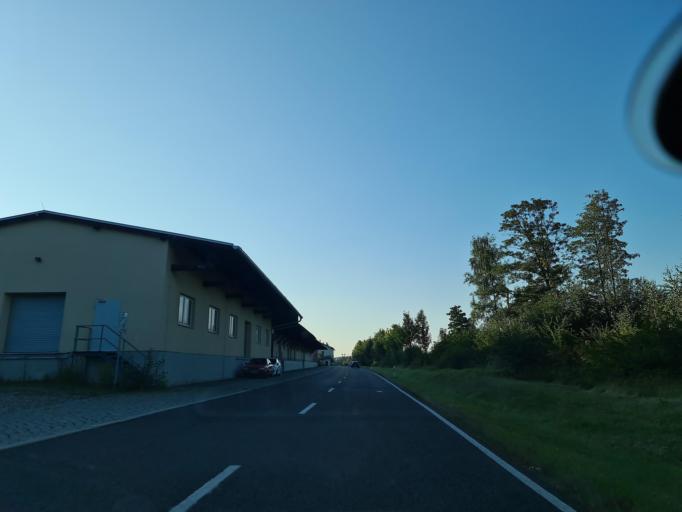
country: DE
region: Saxony
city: Olbernhau
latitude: 50.6548
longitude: 13.3399
